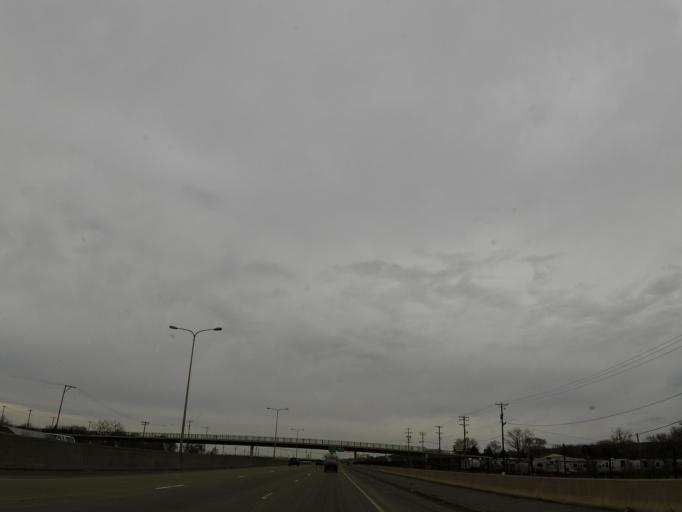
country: US
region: Minnesota
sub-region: Washington County
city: Newport
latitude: 44.8644
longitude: -92.9983
